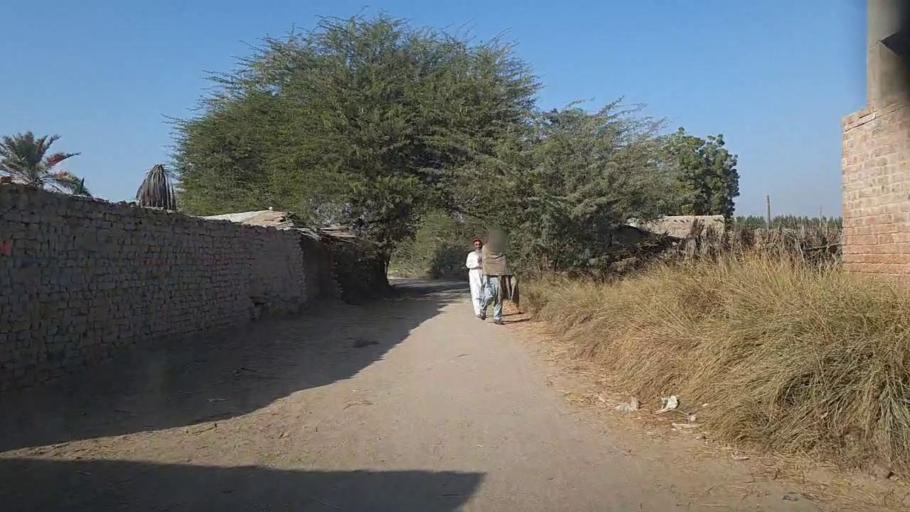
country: PK
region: Sindh
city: Khairpur
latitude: 28.0603
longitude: 69.6950
